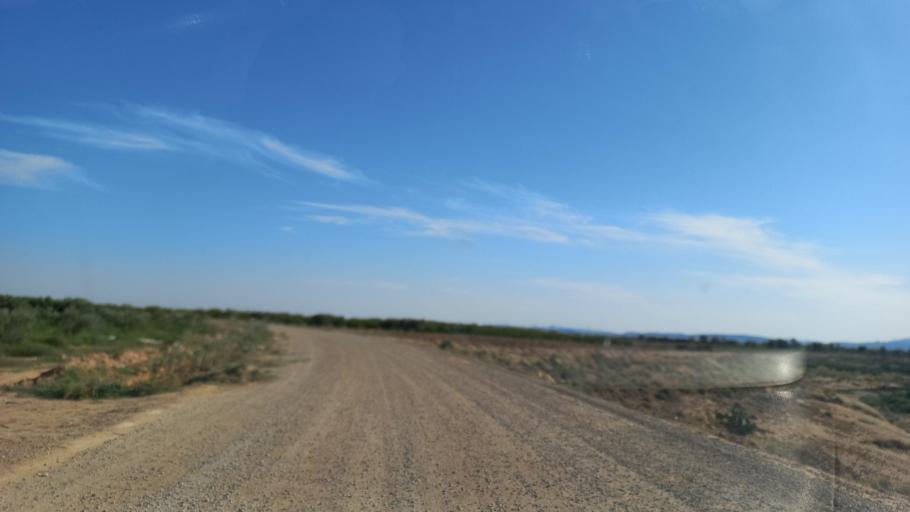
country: TN
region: Al Qasrayn
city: Sbiba
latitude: 35.2984
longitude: 9.0973
